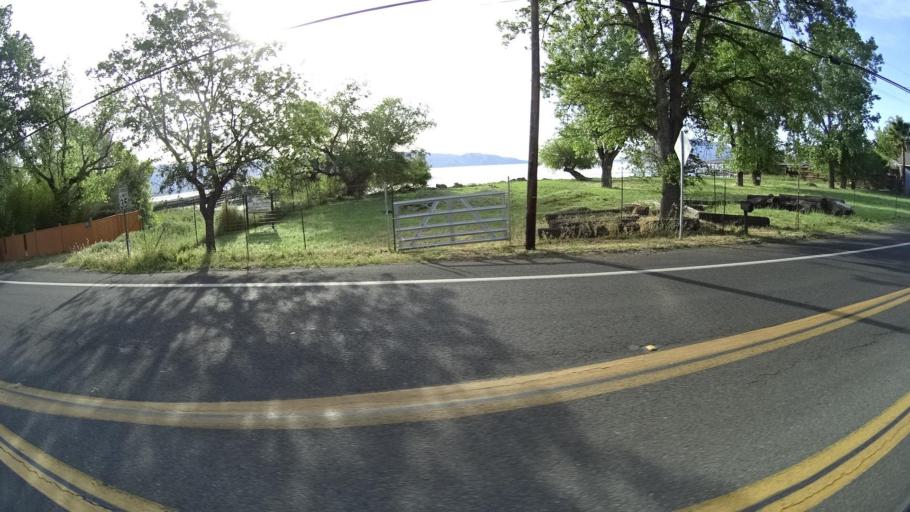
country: US
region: California
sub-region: Lake County
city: North Lakeport
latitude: 39.0905
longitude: -122.9033
